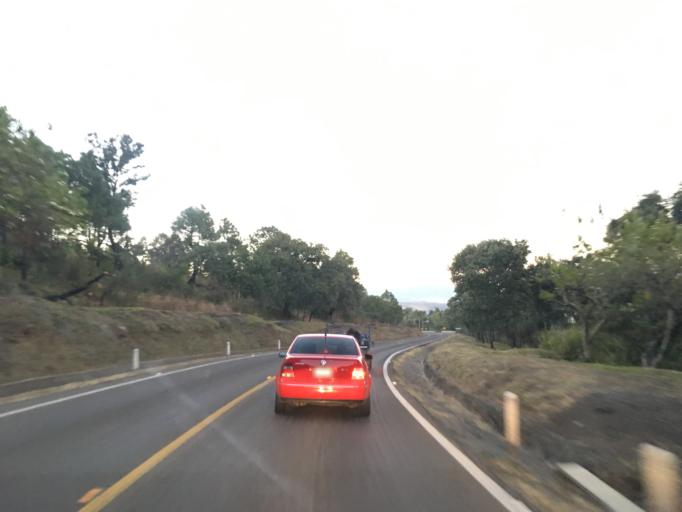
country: MX
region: Michoacan
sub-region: Zinapecuaro
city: Santa Clara del Tule
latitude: 19.8104
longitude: -100.8109
